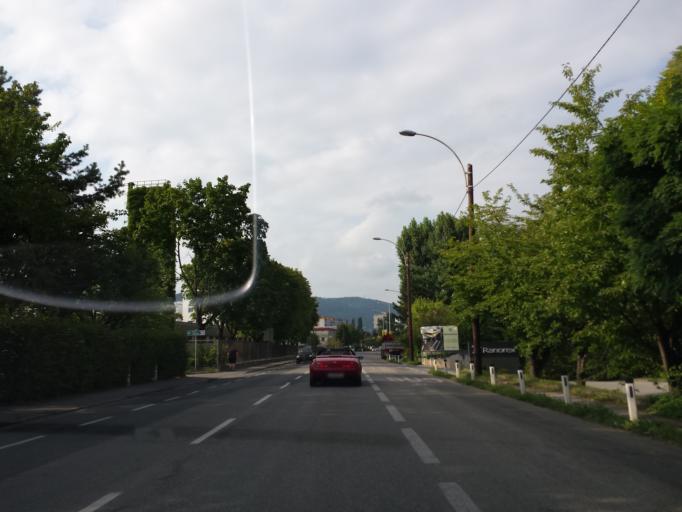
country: AT
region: Styria
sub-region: Graz Stadt
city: Wetzelsdorf
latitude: 47.0442
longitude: 15.3953
